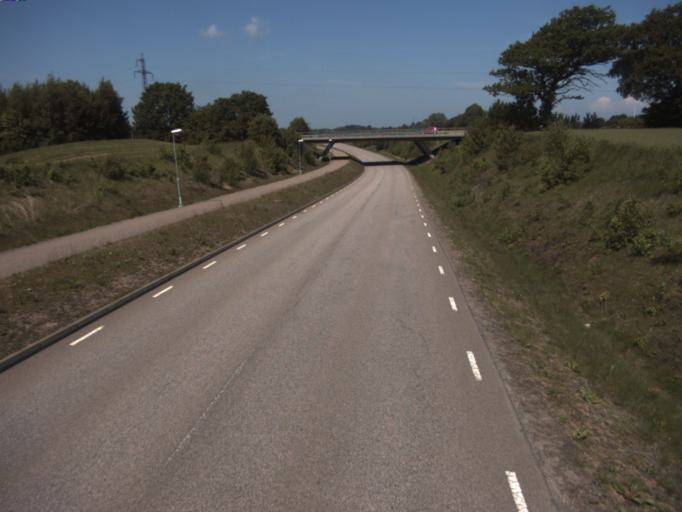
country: SE
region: Skane
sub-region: Helsingborg
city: Barslov
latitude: 56.0135
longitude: 12.8085
